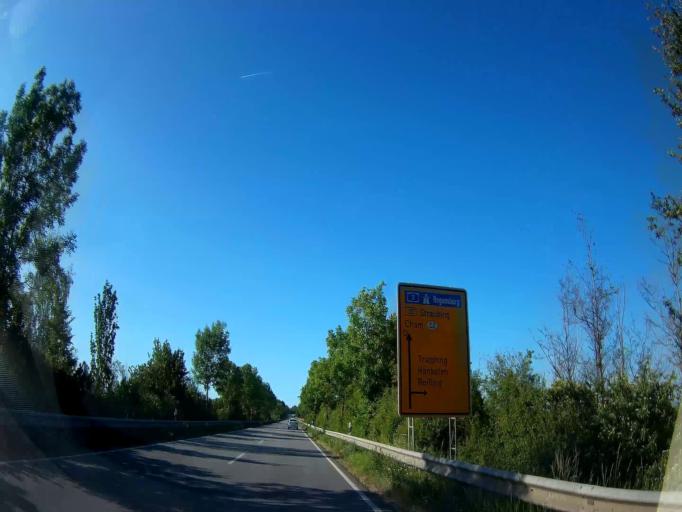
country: DE
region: Bavaria
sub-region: Lower Bavaria
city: Pilsting
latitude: 48.7463
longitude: 12.6600
